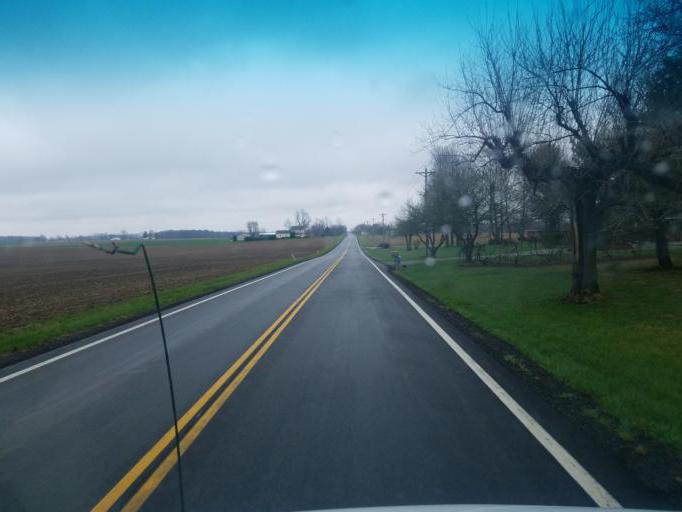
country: US
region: Ohio
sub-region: Huron County
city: Willard
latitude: 40.9600
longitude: -82.8034
